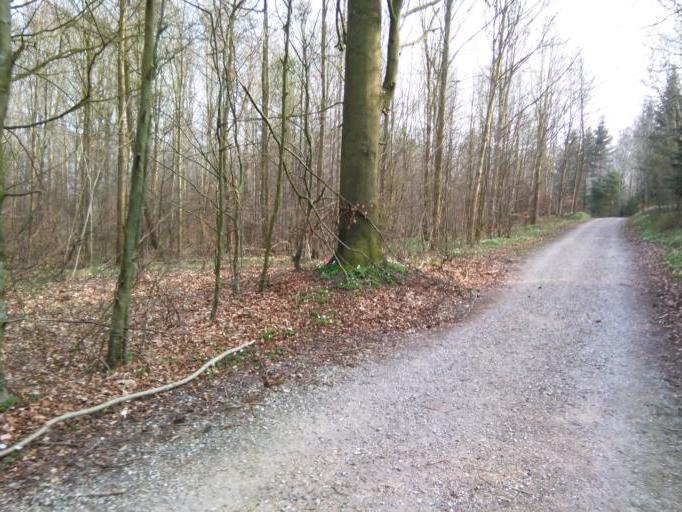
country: DK
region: Central Jutland
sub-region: Arhus Kommune
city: Beder
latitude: 56.0702
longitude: 10.2462
